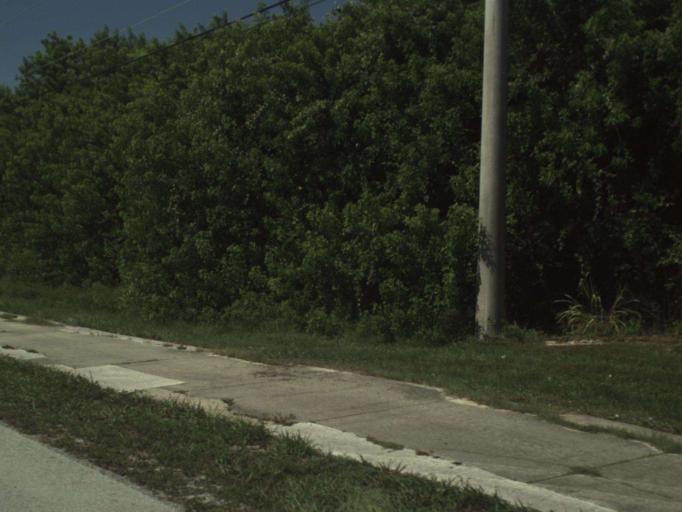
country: US
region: Florida
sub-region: Indian River County
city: South Beach
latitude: 27.5688
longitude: -80.3275
